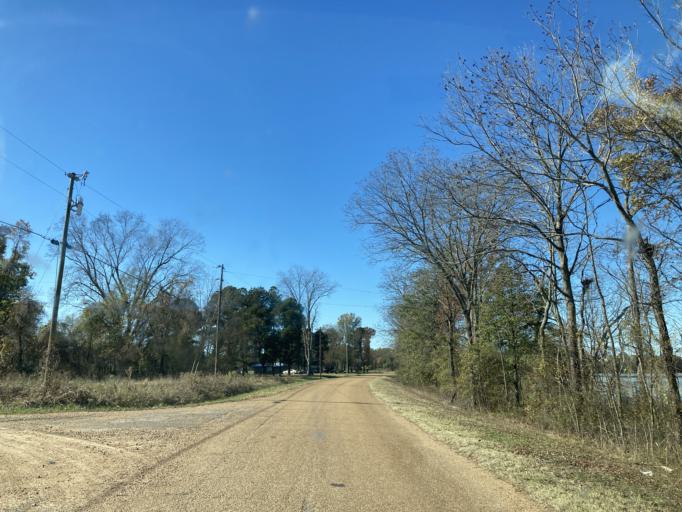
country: US
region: Mississippi
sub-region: Hinds County
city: Lynchburg
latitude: 32.6389
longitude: -90.6123
